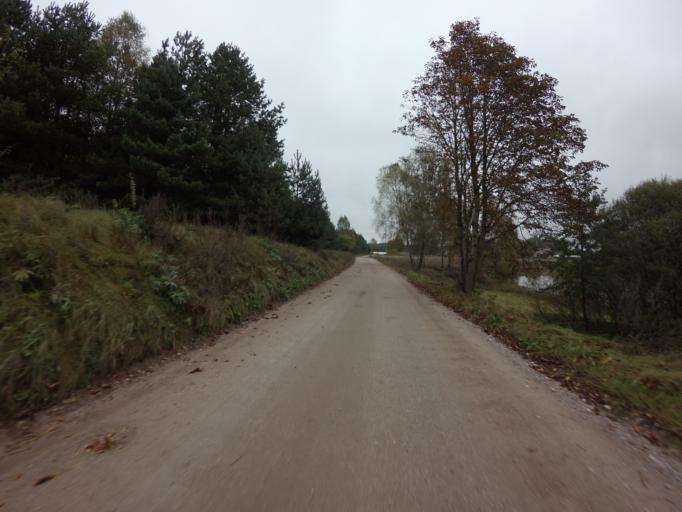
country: PL
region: Pomeranian Voivodeship
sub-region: Powiat kartuski
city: Stezyca
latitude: 54.1663
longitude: 17.9280
